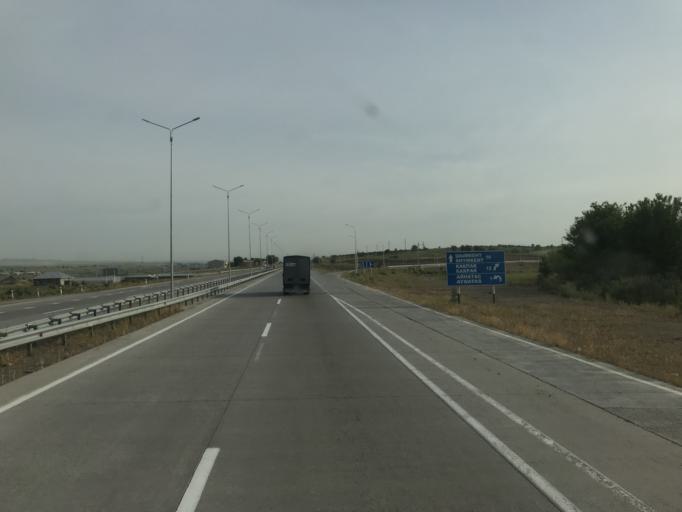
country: KZ
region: Ongtustik Qazaqstan
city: Qazyqurt
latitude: 41.6840
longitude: 69.3939
